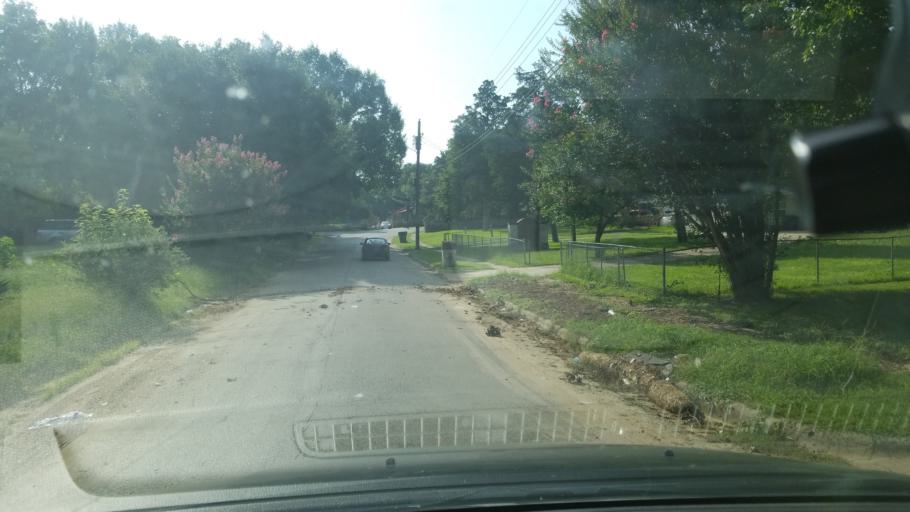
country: US
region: Texas
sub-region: Dallas County
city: Hutchins
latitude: 32.7147
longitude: -96.6927
